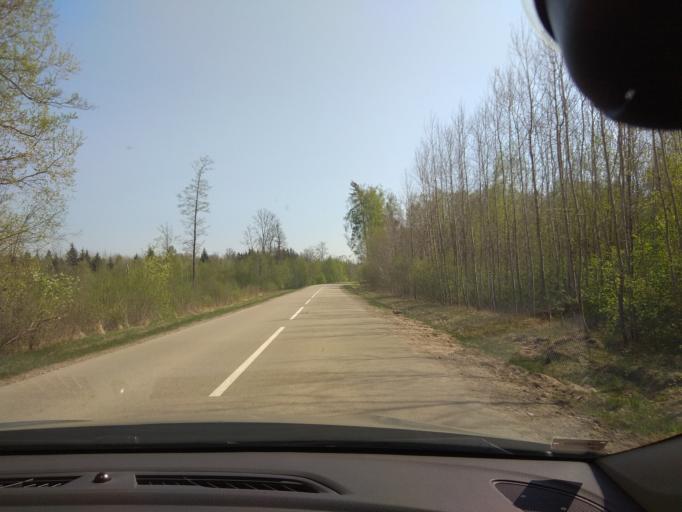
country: LT
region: Panevezys
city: Pasvalys
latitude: 55.9792
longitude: 24.1876
